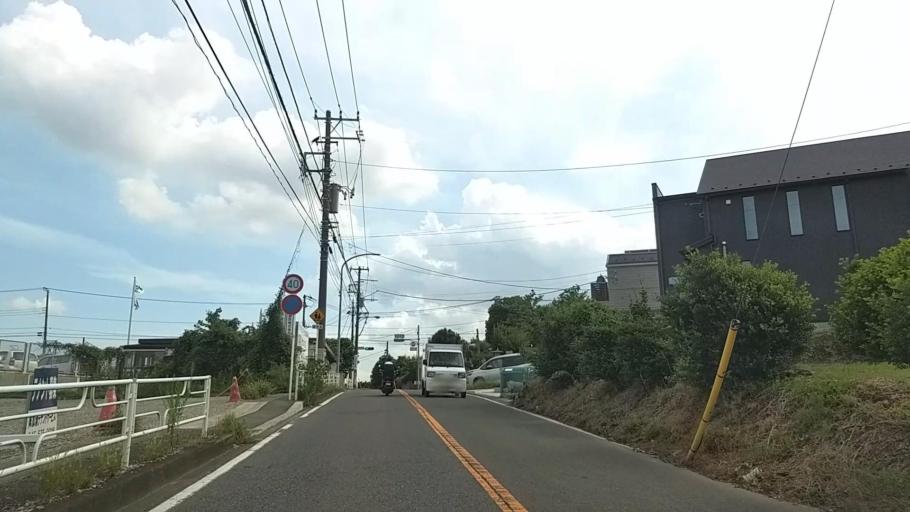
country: JP
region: Kanagawa
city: Yokohama
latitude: 35.4972
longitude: 139.5833
